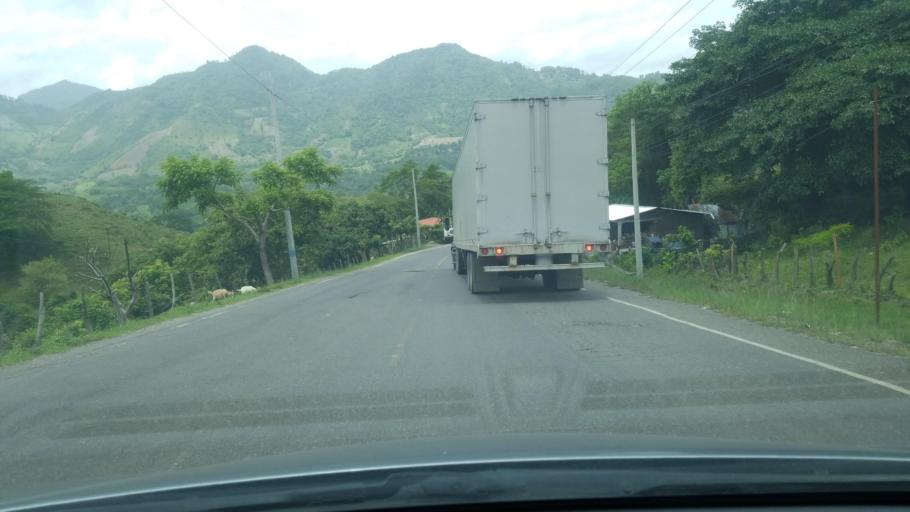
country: HN
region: Copan
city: Santa Rosa de Copan
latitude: 14.7227
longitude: -88.7701
